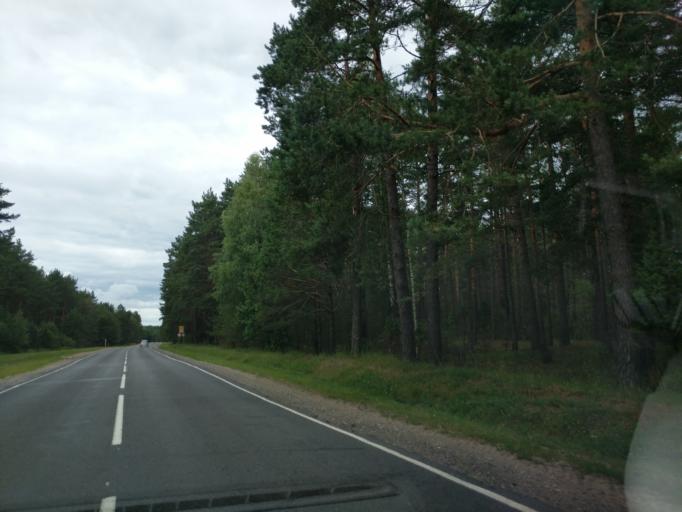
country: BY
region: Minsk
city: Myadzyel
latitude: 54.8382
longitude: 26.9321
